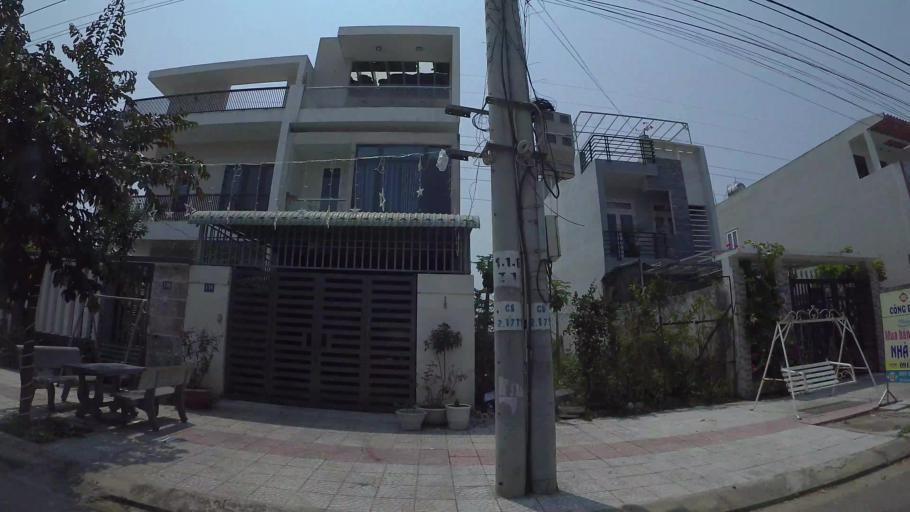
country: VN
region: Da Nang
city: Cam Le
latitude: 16.0200
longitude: 108.2264
